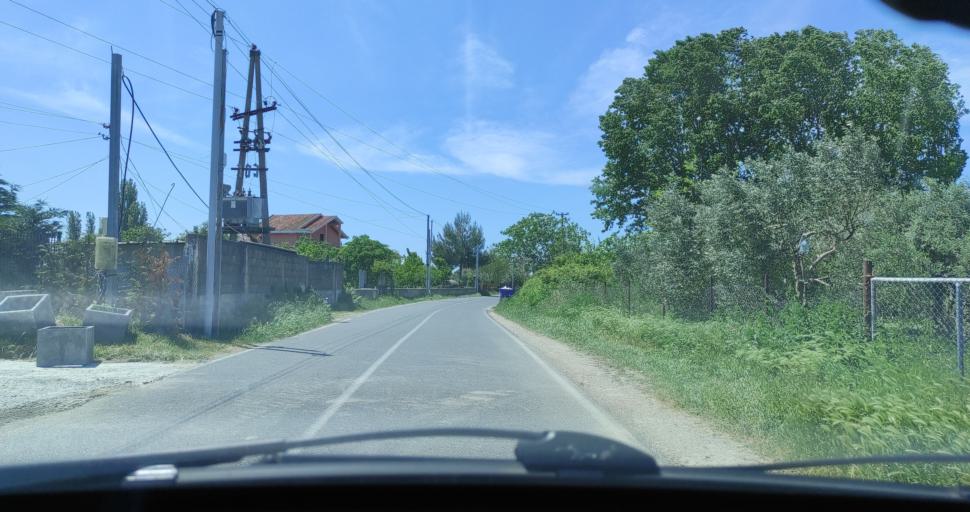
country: AL
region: Lezhe
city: Lezhe
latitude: 41.7601
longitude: 19.6290
